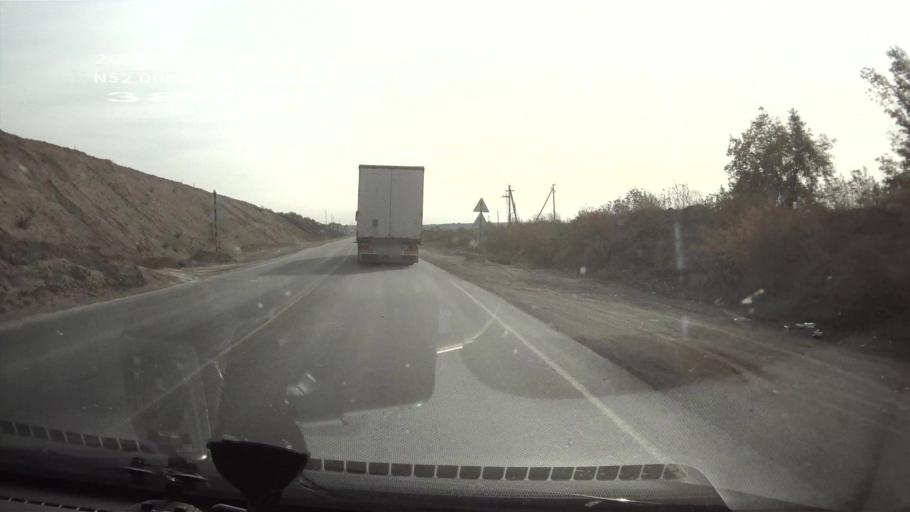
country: RU
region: Saratov
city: Sinodskoye
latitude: 52.0093
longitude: 46.6868
